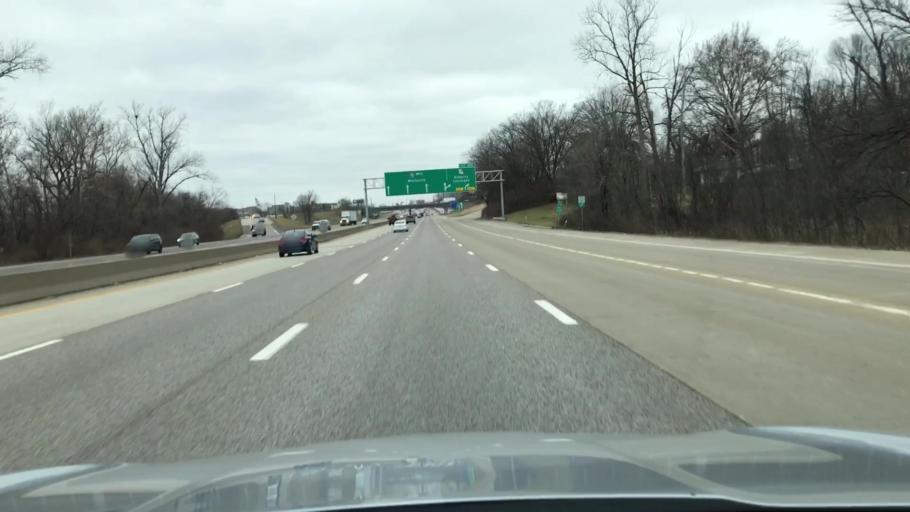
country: US
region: Missouri
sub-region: Saint Charles County
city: Saint Peters
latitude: 38.8008
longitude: -90.6451
